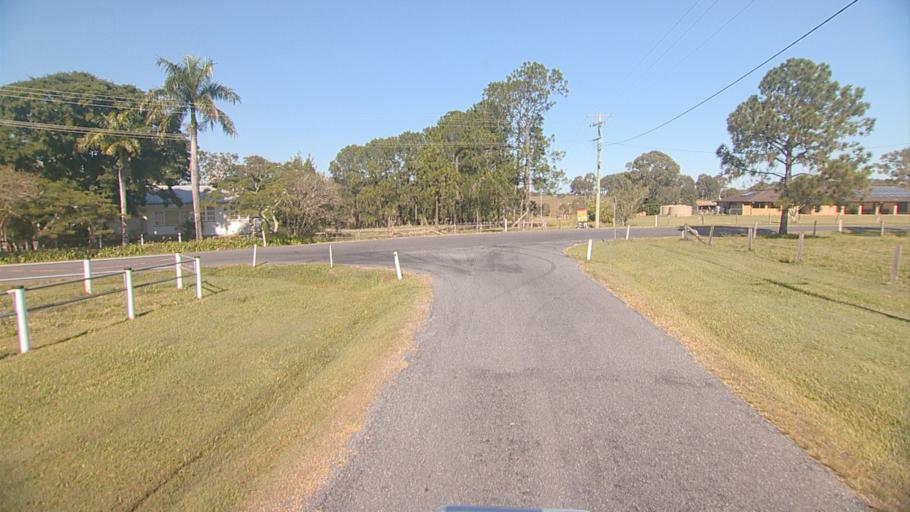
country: AU
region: Queensland
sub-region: Gold Coast
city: Yatala
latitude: -27.6878
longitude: 153.2242
